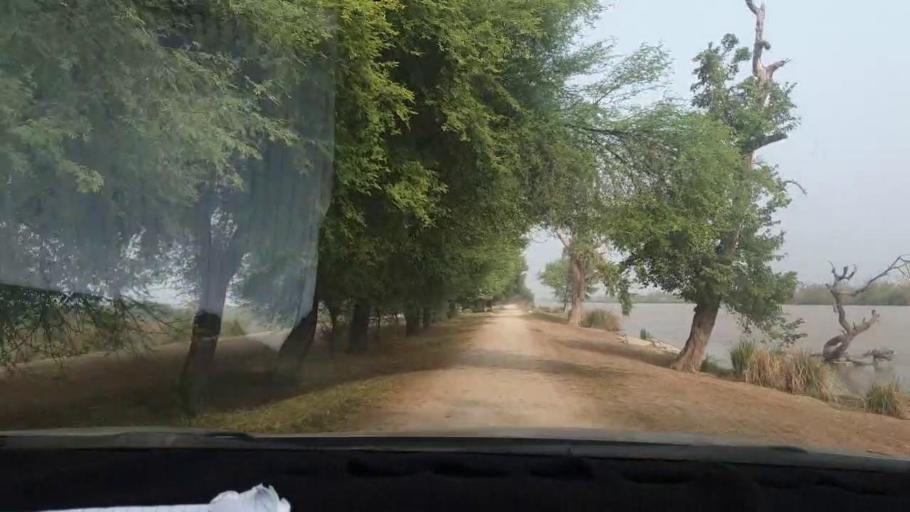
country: PK
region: Sindh
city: Tando Adam
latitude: 25.6792
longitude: 68.5568
